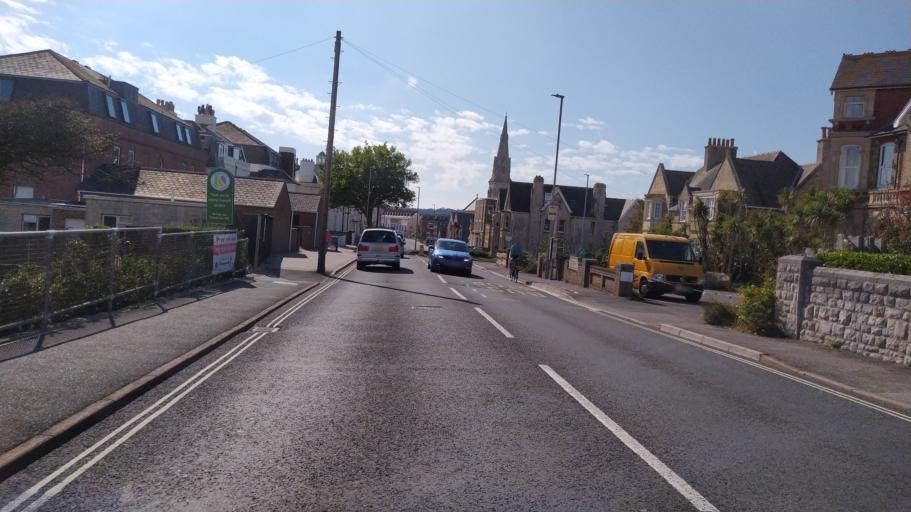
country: GB
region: England
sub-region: Dorset
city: Weymouth
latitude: 50.6207
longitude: -2.4487
